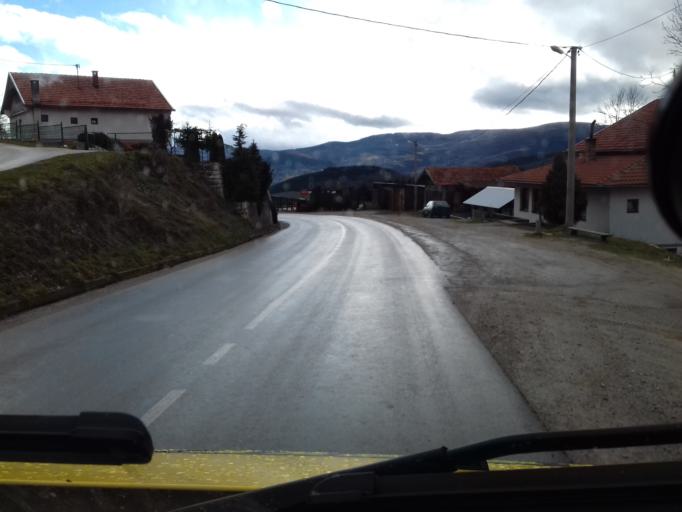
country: BA
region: Federation of Bosnia and Herzegovina
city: Turbe
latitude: 44.2681
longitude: 17.5249
